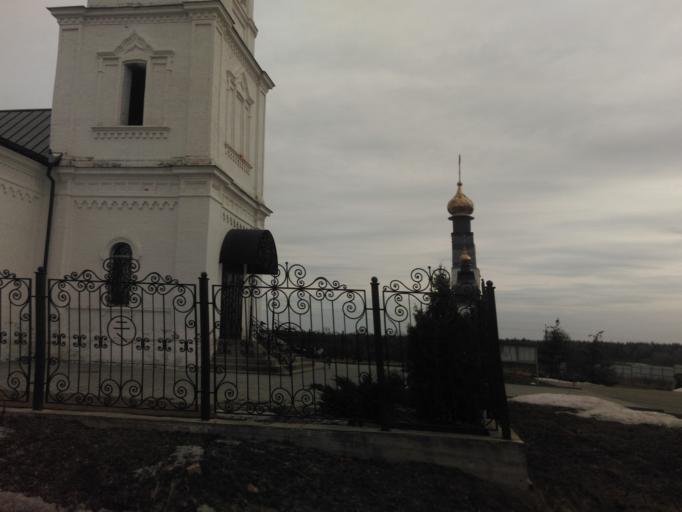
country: RU
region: Moskovskaya
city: Kolyubakino
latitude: 55.6988
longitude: 36.5925
